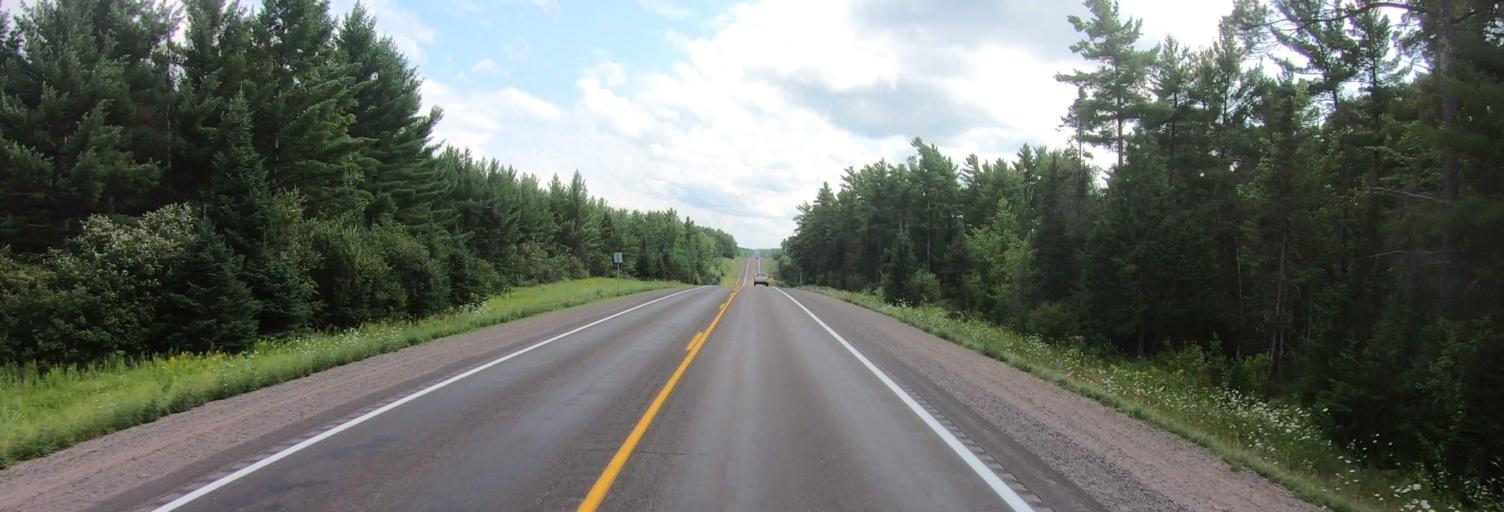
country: US
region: Michigan
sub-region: Ontonagon County
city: Ontonagon
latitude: 46.5589
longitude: -89.1786
